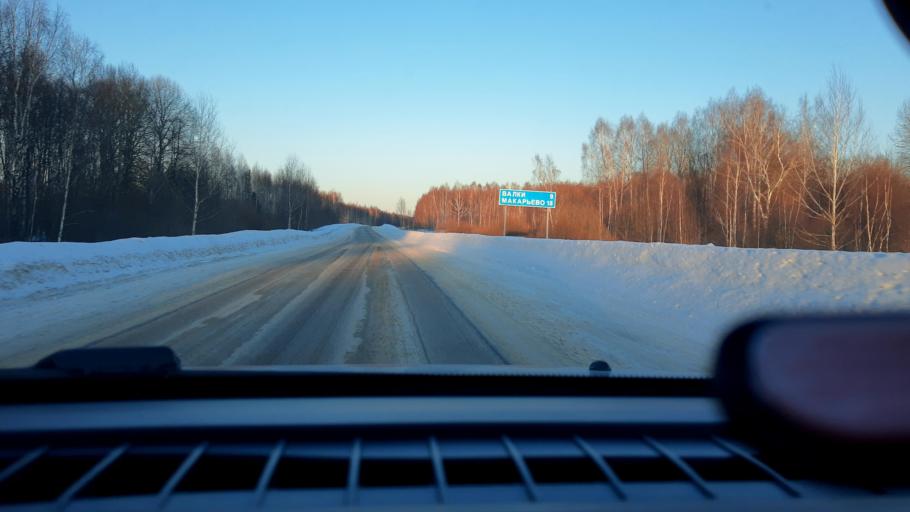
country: RU
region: Nizjnij Novgorod
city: Pervoye Maya
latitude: 56.1550
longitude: 44.8822
